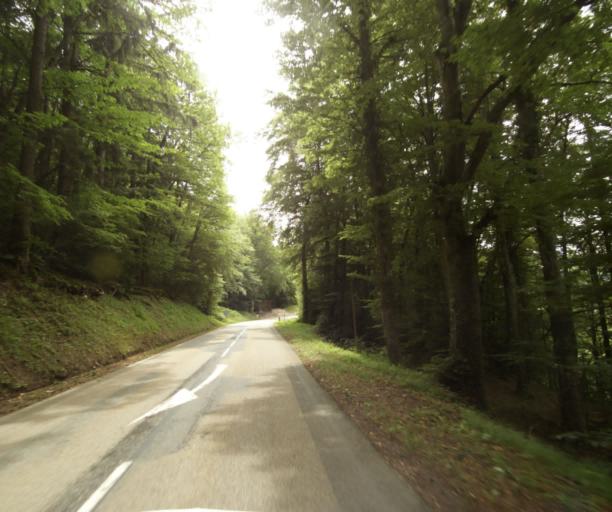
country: FR
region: Rhone-Alpes
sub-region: Departement de la Haute-Savoie
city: Perrignier
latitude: 46.2980
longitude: 6.4645
